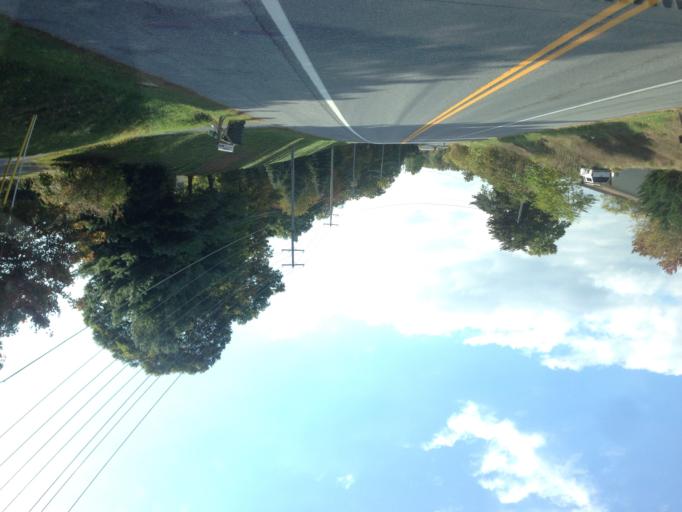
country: US
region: Maryland
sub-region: Carroll County
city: Mount Airy
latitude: 39.3596
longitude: -77.1564
